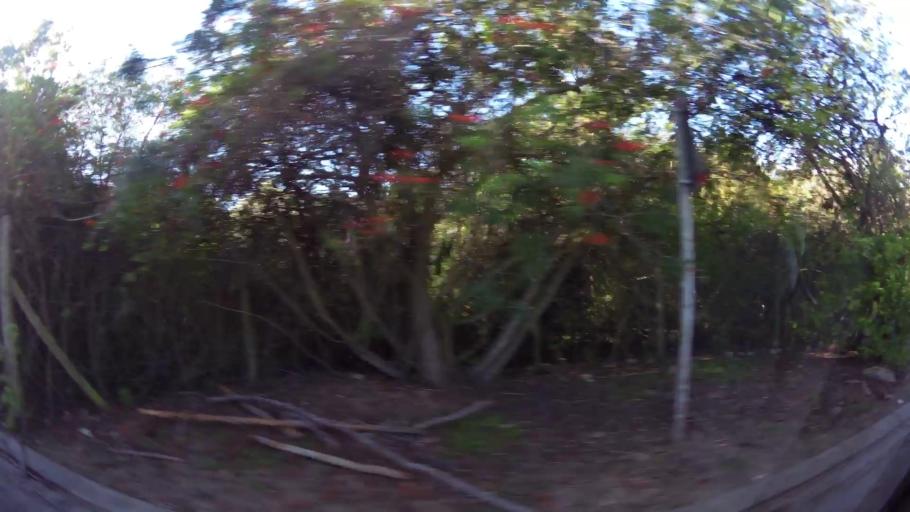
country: ZA
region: Western Cape
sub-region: Eden District Municipality
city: Knysna
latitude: -34.0341
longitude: 23.0196
